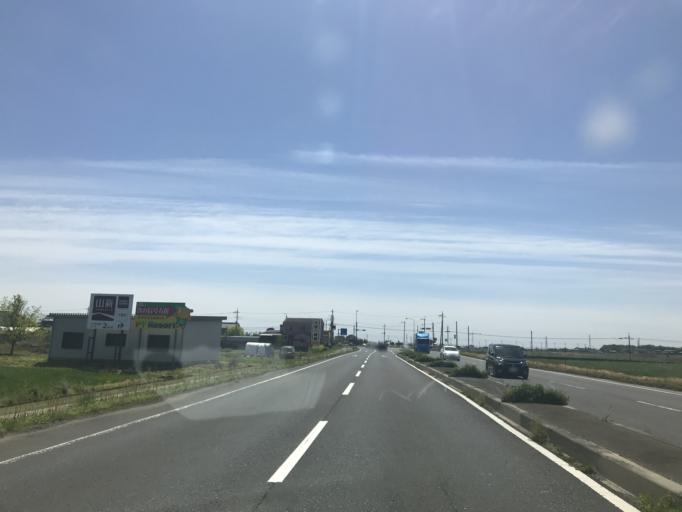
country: JP
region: Ibaraki
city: Ishige
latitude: 36.2039
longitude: 139.9843
